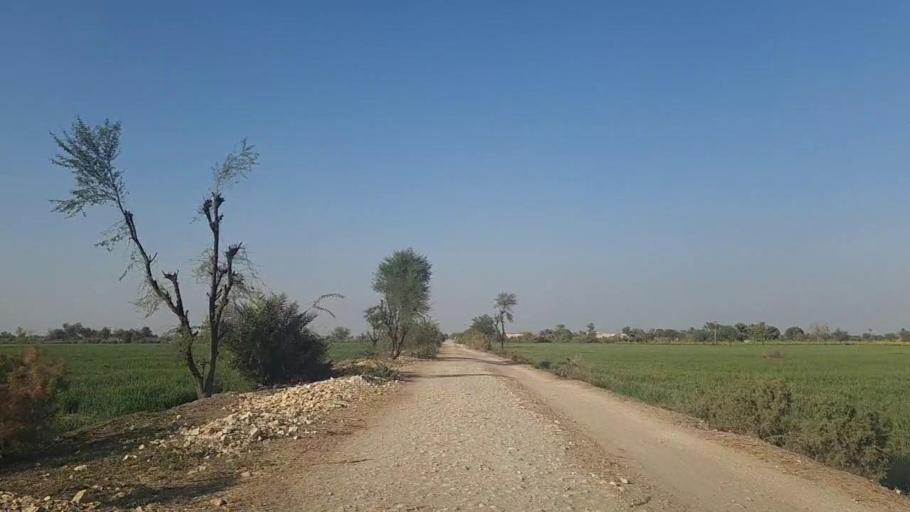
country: PK
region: Sindh
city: Jam Sahib
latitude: 26.3159
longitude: 68.7149
